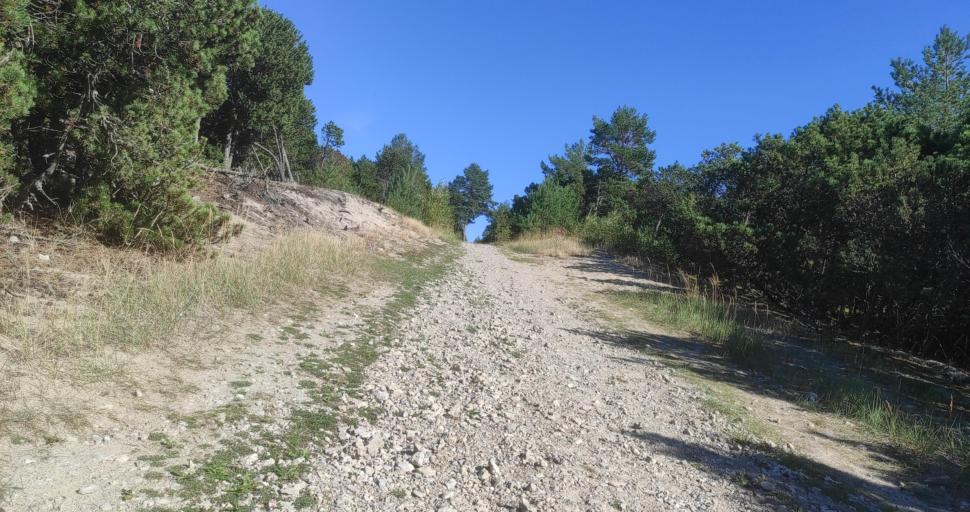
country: LT
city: Neringa
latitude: 55.3541
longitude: 21.0300
